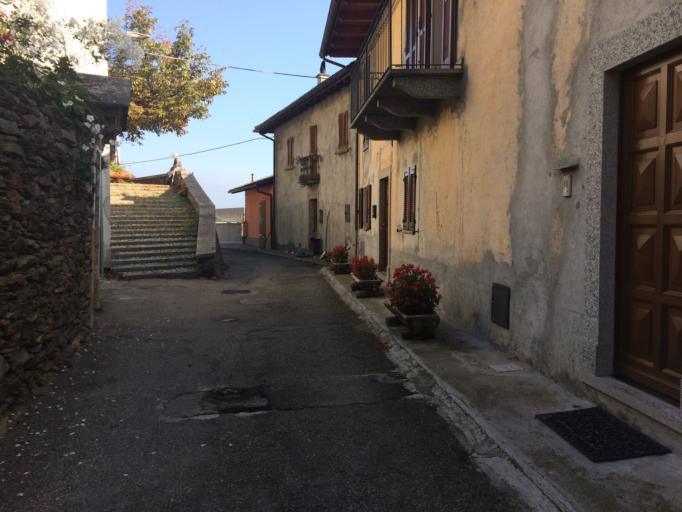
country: IT
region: Piedmont
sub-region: Provincia Verbano-Cusio-Ossola
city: Cavaglio-Spoccia
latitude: 46.0690
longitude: 8.6455
